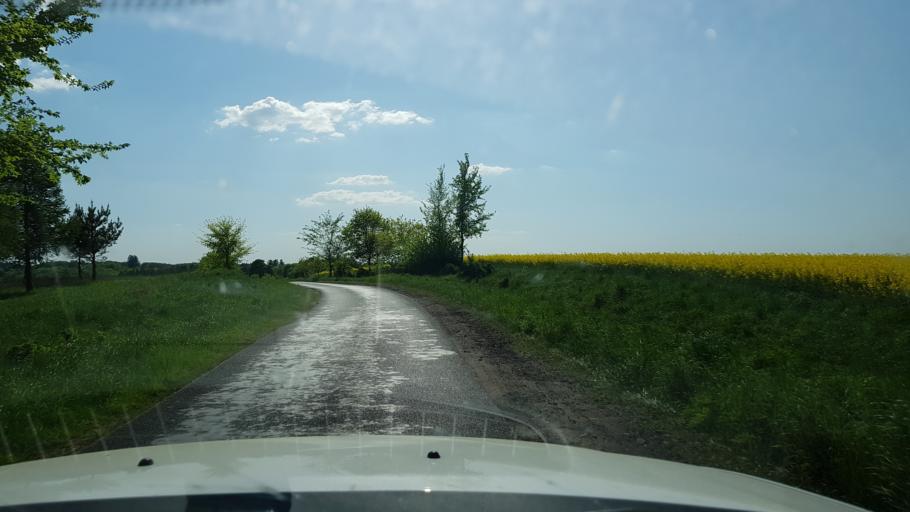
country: PL
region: West Pomeranian Voivodeship
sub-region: Powiat kolobrzeski
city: Goscino
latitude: 54.0190
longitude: 15.6269
